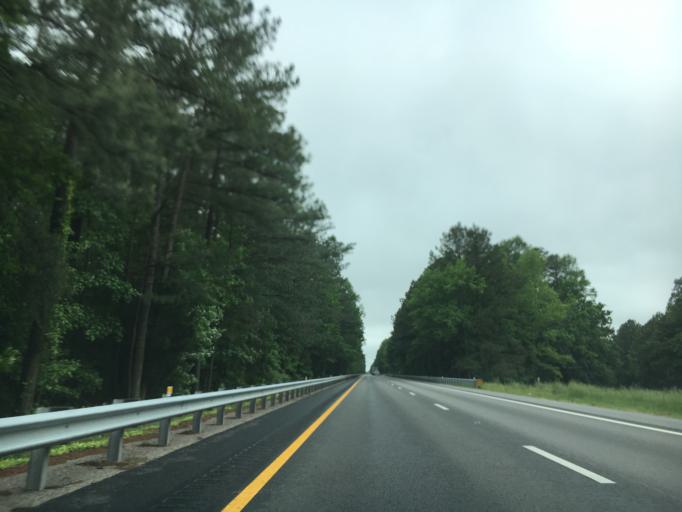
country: US
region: Virginia
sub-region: Dinwiddie County
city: Dinwiddie
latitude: 37.0384
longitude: -77.6278
